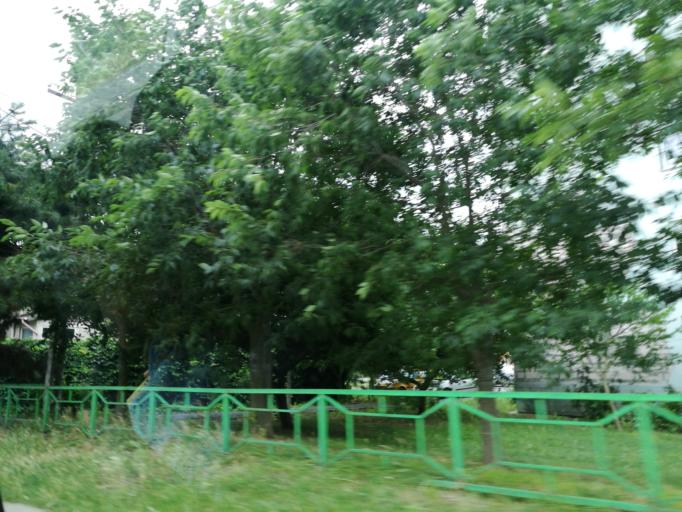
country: RO
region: Constanta
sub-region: Municipiul Mangalia
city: Mangalia
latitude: 43.8137
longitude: 28.5728
